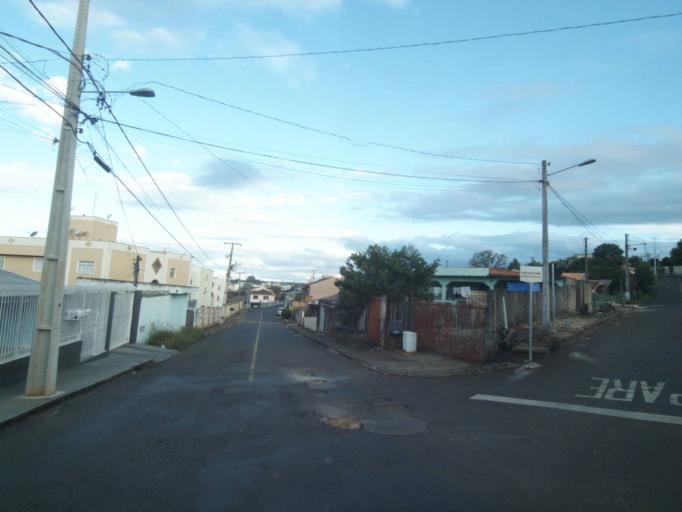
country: BR
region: Parana
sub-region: Telemaco Borba
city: Telemaco Borba
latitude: -24.3270
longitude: -50.6400
